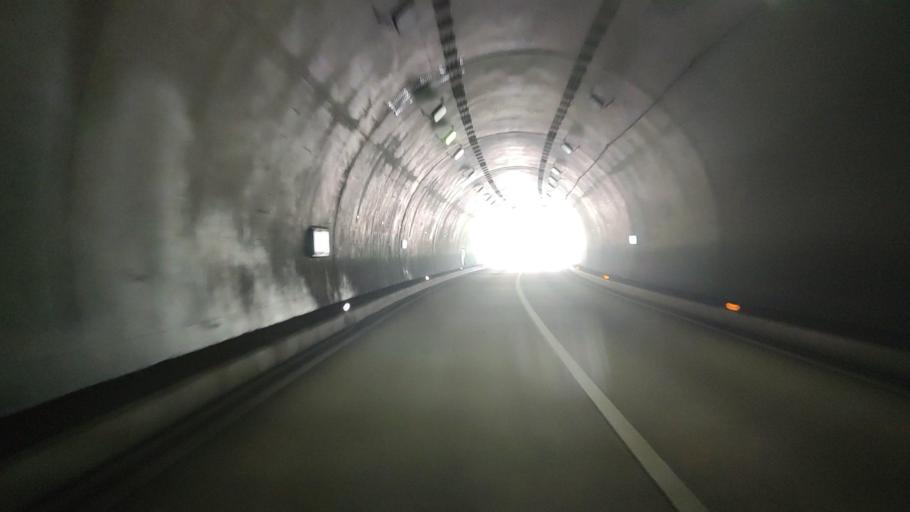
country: JP
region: Wakayama
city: Shingu
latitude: 33.8597
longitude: 135.8521
